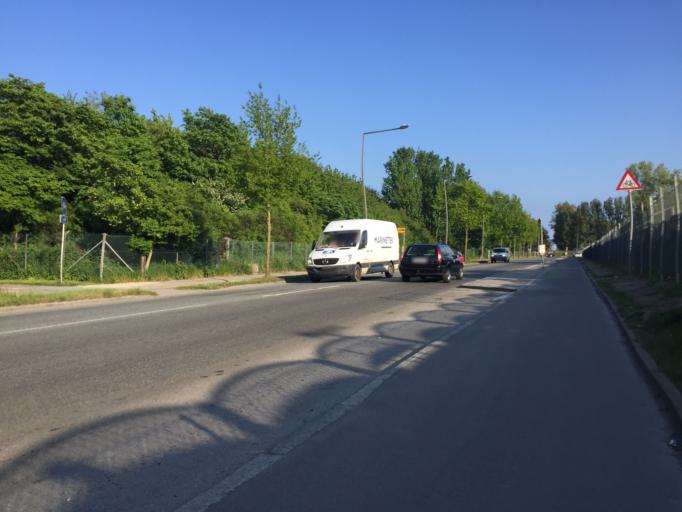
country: DK
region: Capital Region
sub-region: Kobenhavn
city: Christianshavn
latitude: 55.6787
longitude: 12.6173
